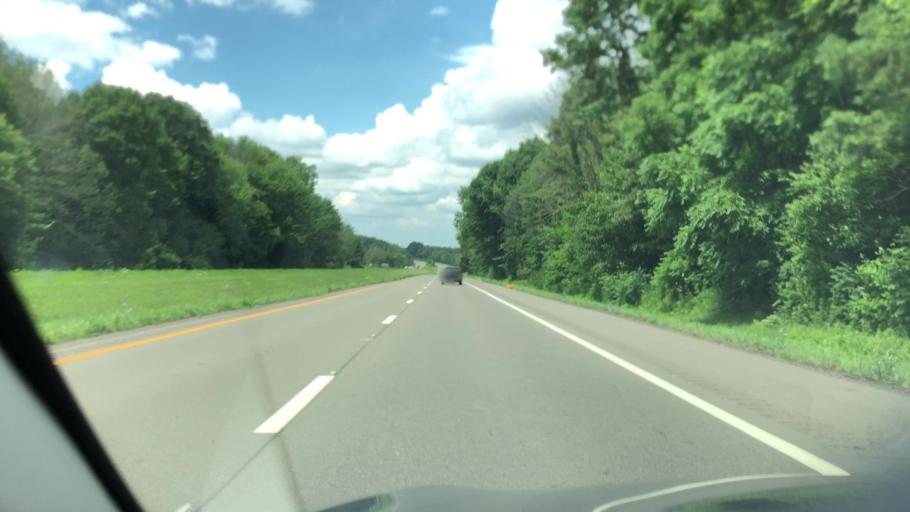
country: US
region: Ohio
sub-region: Stark County
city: Massillon
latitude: 40.8399
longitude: -81.5528
